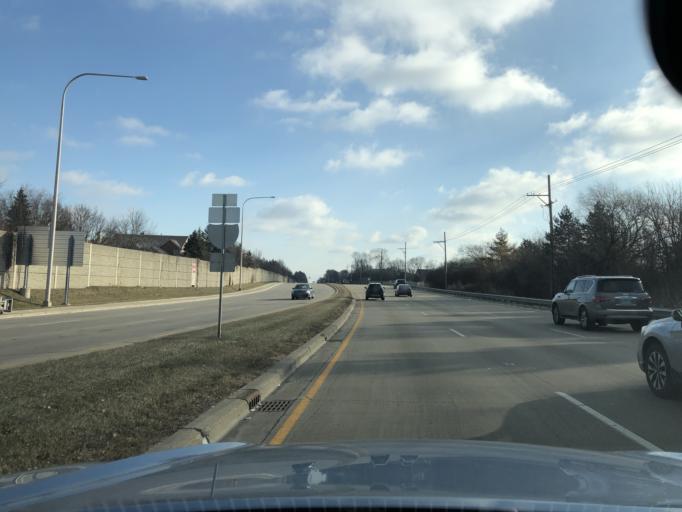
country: US
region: Illinois
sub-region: Cook County
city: Northbrook
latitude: 42.1059
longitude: -87.8655
